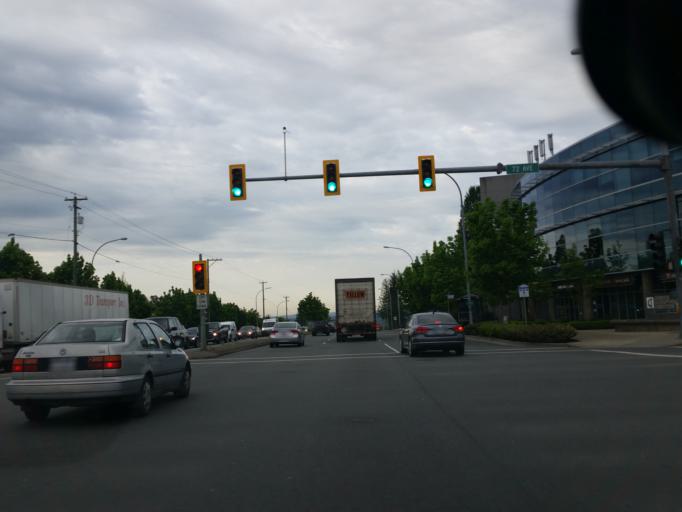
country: CA
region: British Columbia
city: Langley
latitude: 49.1337
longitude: -122.6685
